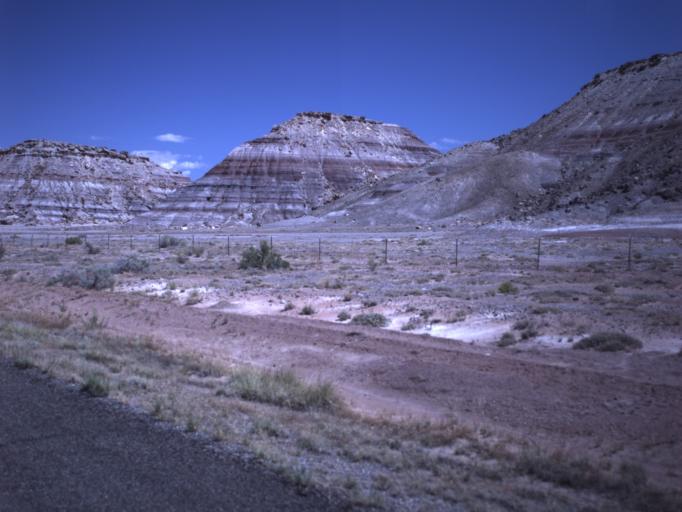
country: US
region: Utah
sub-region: Carbon County
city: East Carbon City
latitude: 38.9115
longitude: -110.3711
